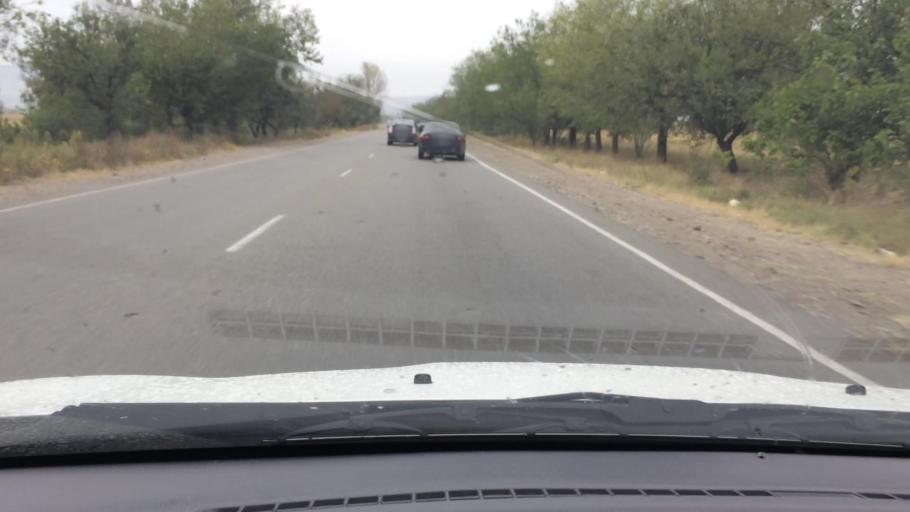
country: GE
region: Kvemo Kartli
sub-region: Marneuli
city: Marneuli
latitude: 41.5649
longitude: 44.7756
